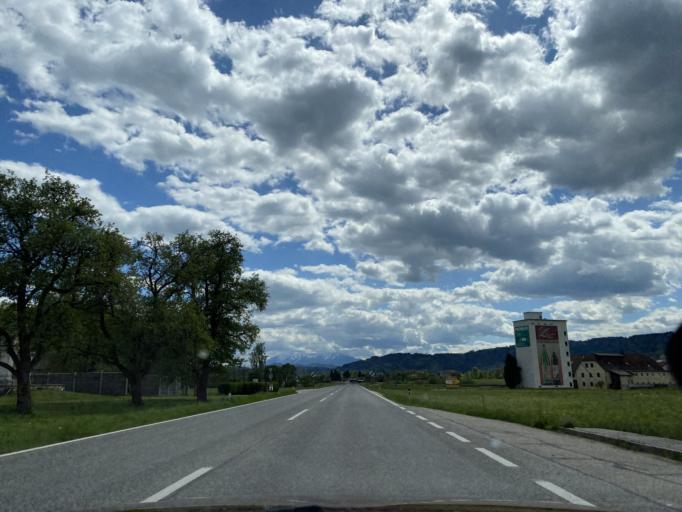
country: AT
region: Carinthia
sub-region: Politischer Bezirk Wolfsberg
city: Sankt Andrae
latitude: 46.7991
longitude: 14.8279
